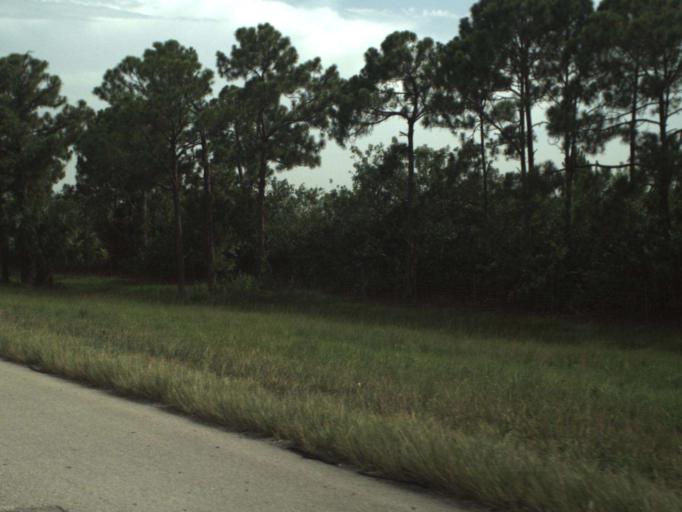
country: US
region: Florida
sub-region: Saint Lucie County
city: Port Saint Lucie
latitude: 27.2518
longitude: -80.4177
